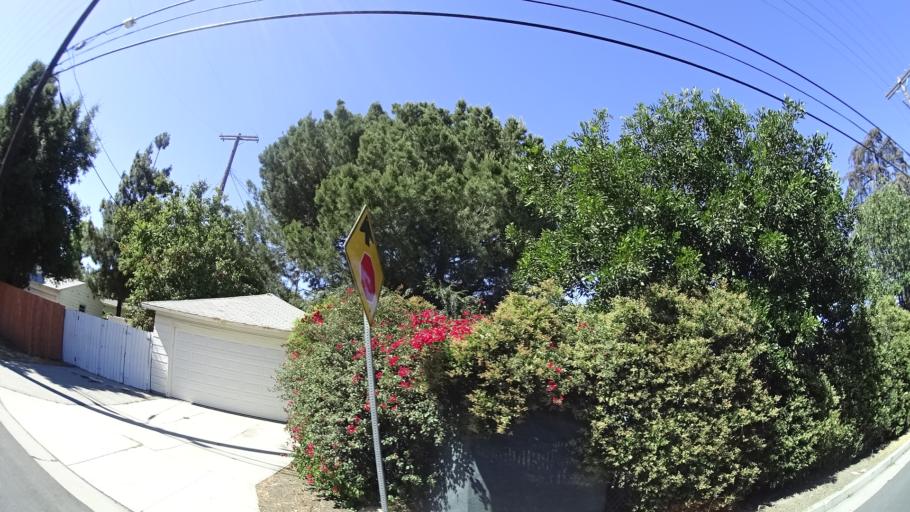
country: US
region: California
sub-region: Los Angeles County
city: Sherman Oaks
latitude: 34.1545
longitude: -118.4642
